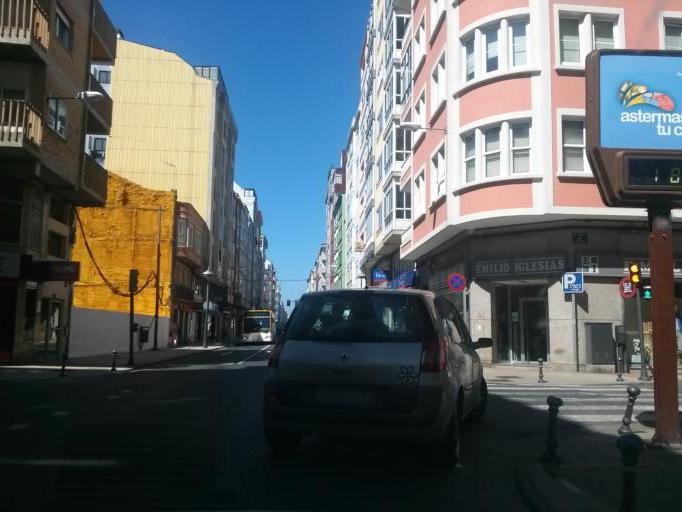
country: ES
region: Galicia
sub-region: Provincia de Lugo
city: Lugo
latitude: 43.0165
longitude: -7.5599
